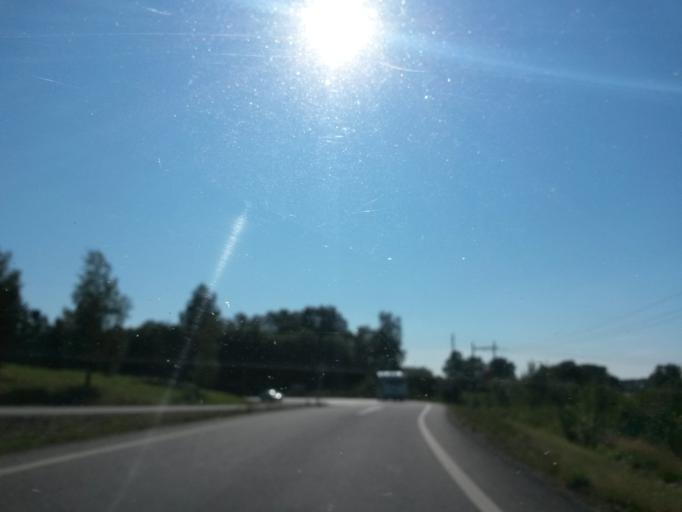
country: SE
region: Vaestra Goetaland
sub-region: Vargarda Kommun
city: Vargarda
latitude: 58.0240
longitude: 12.7825
